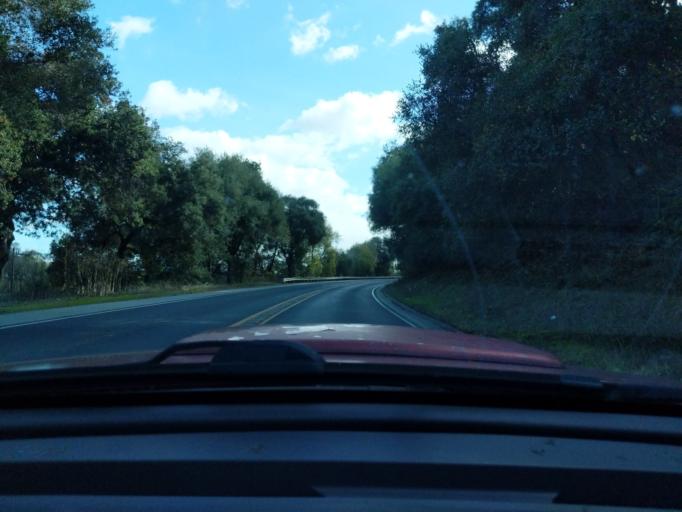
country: US
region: California
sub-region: San Benito County
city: San Juan Bautista
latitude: 36.8921
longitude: -121.5684
